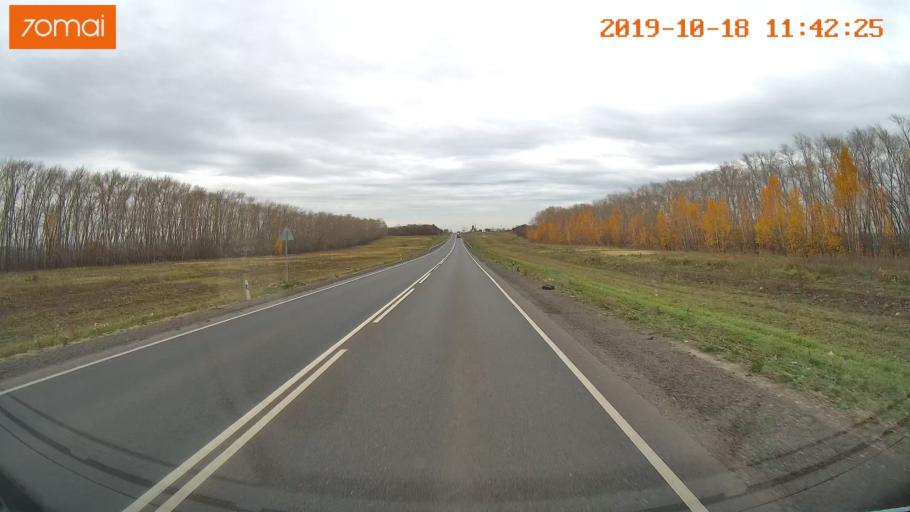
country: RU
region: Rjazan
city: Oktyabr'skiy
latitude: 54.1880
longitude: 38.9272
